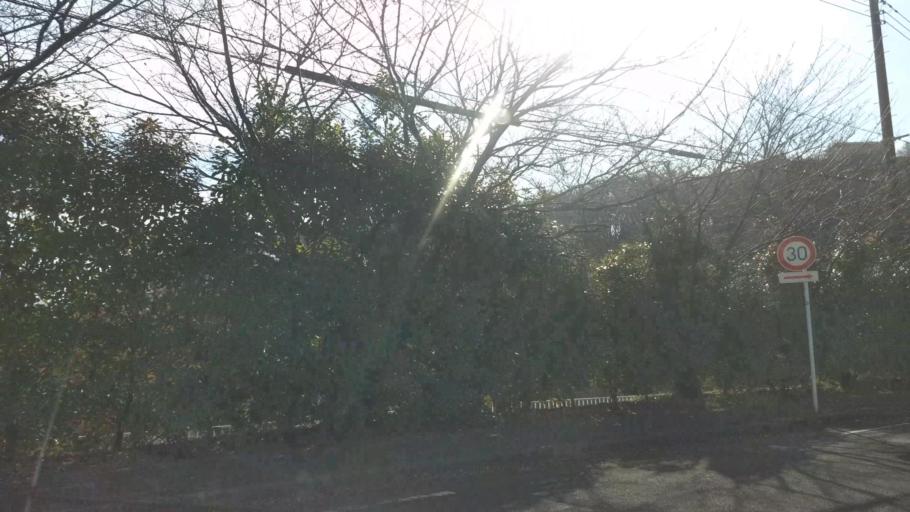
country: JP
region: Kanagawa
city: Hadano
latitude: 35.3578
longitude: 139.2317
